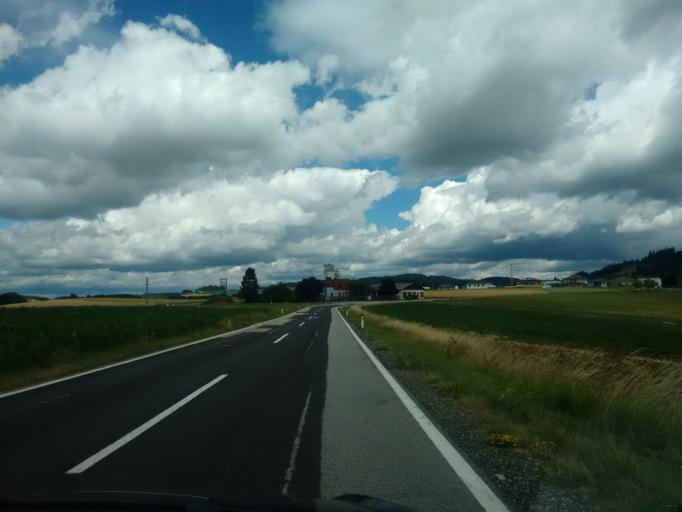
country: AT
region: Upper Austria
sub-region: Politischer Bezirk Urfahr-Umgebung
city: Herzogsdorf
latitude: 48.4218
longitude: 14.1592
